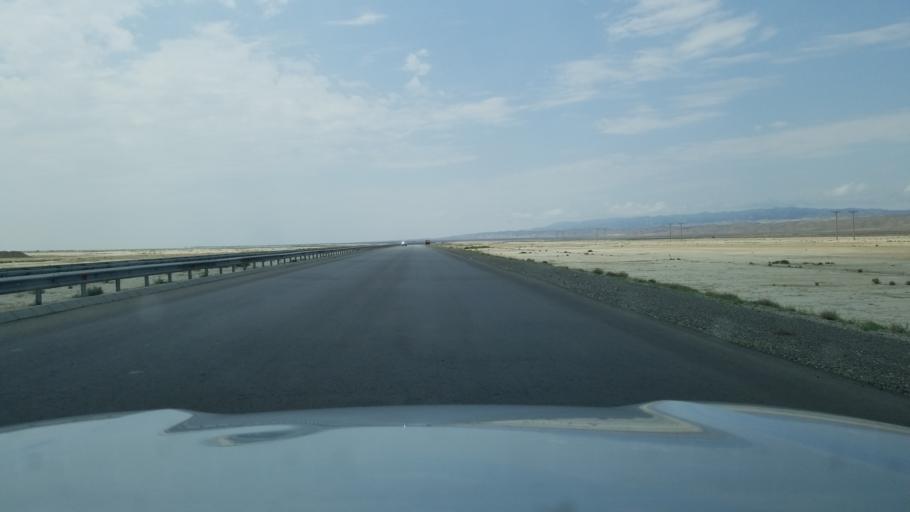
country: TM
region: Balkan
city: Gazanjyk
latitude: 39.2770
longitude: 55.1850
